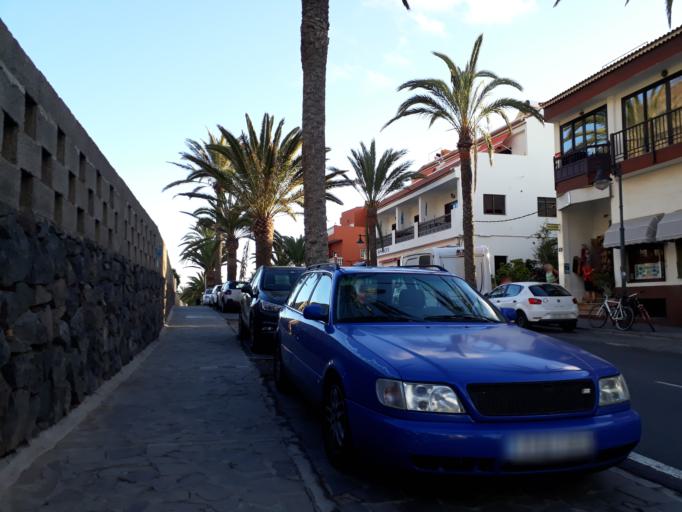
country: ES
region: Canary Islands
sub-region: Provincia de Santa Cruz de Tenerife
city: Alajero
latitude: 28.0880
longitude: -17.3390
